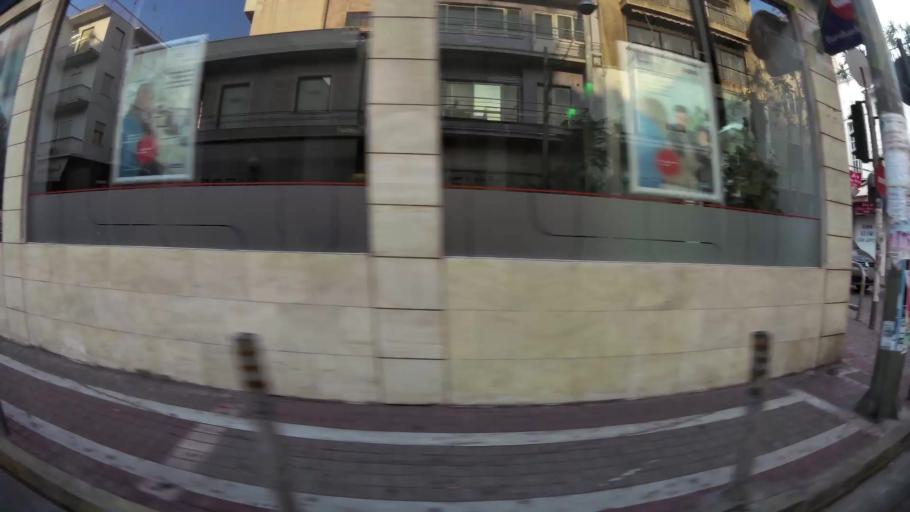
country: GR
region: Attica
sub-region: Nomarchia Athinas
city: Dhafni
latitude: 37.9519
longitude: 23.7373
